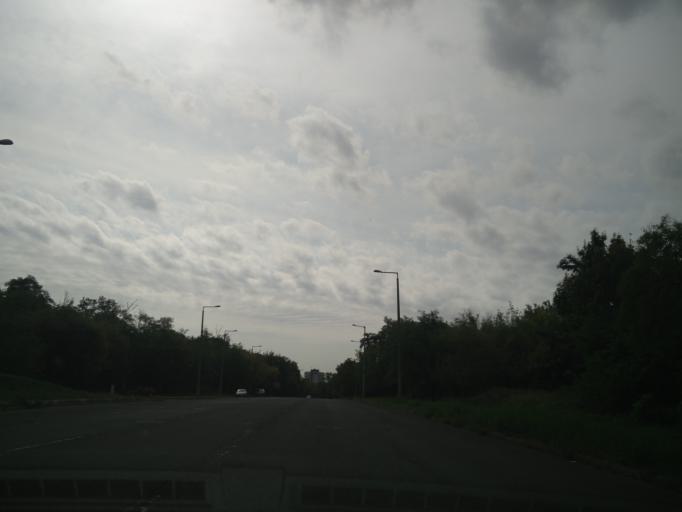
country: HU
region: Budapest
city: Budapest XV. keruelet
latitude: 47.5858
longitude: 19.1037
